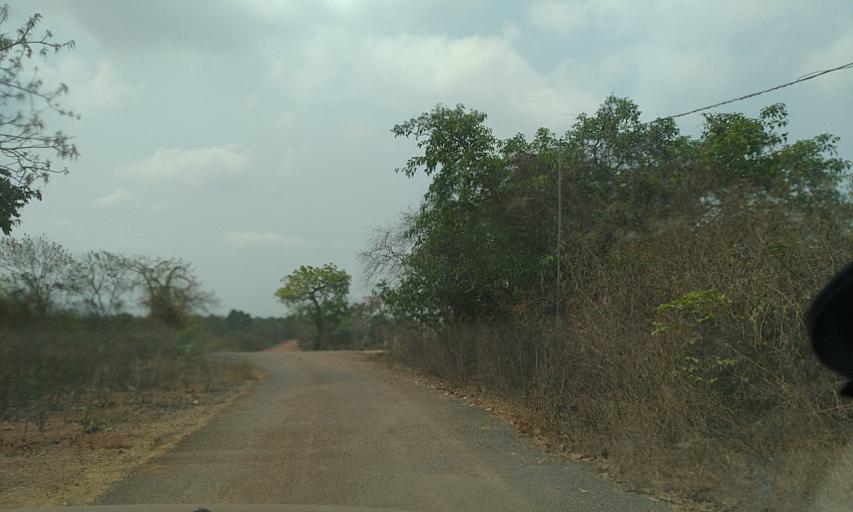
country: IN
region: Goa
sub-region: North Goa
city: Goa Velha
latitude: 15.4792
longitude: 73.9101
